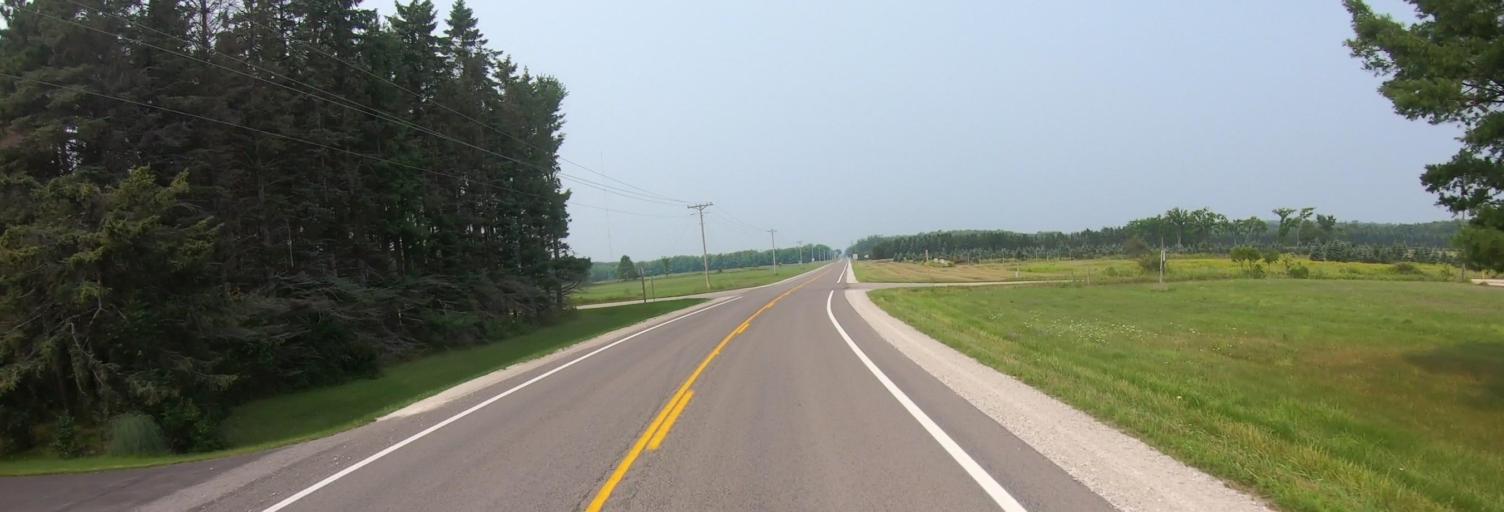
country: US
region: Michigan
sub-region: Chippewa County
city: Sault Ste. Marie
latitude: 46.0431
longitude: -84.0924
